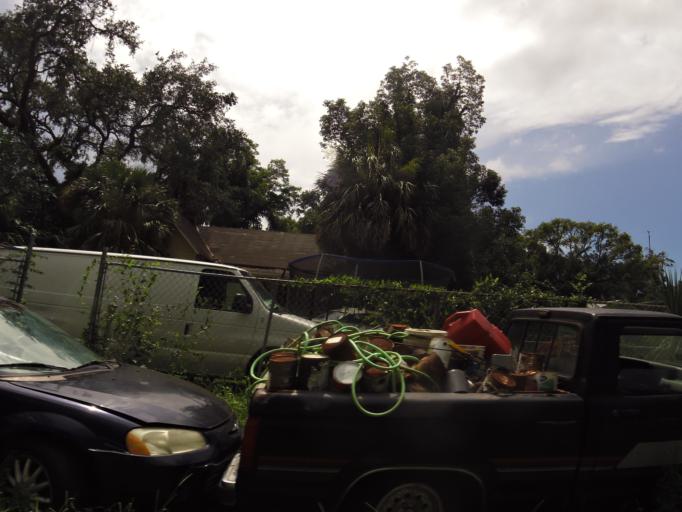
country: US
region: Florida
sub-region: Duval County
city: Jacksonville
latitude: 30.3871
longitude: -81.6407
